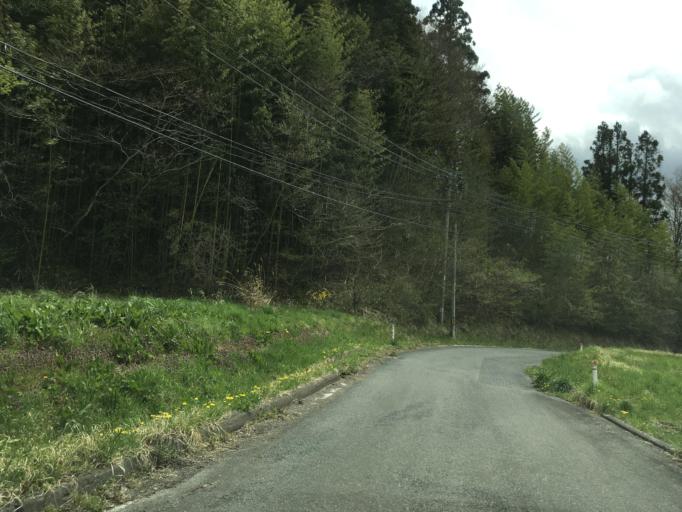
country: JP
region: Iwate
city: Ichinoseki
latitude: 38.8560
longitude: 141.3206
